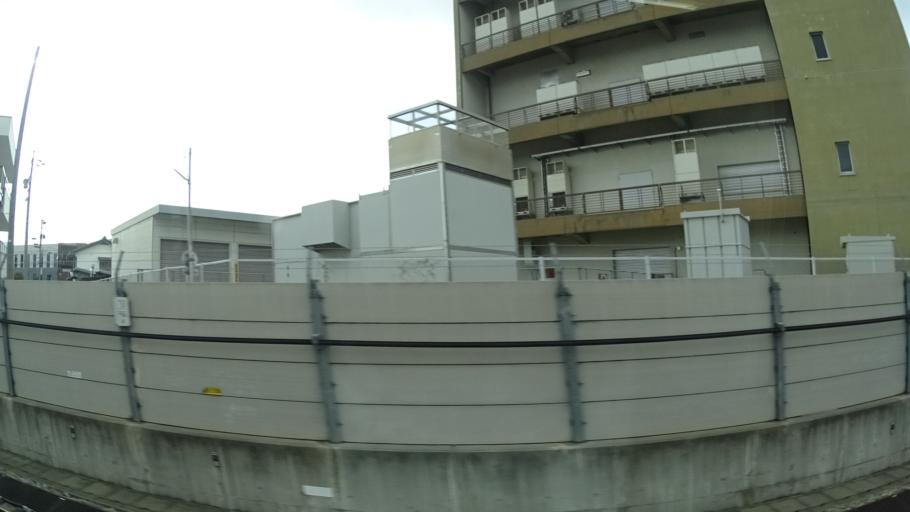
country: JP
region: Nagano
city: Nagano-shi
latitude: 36.6595
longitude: 138.2131
